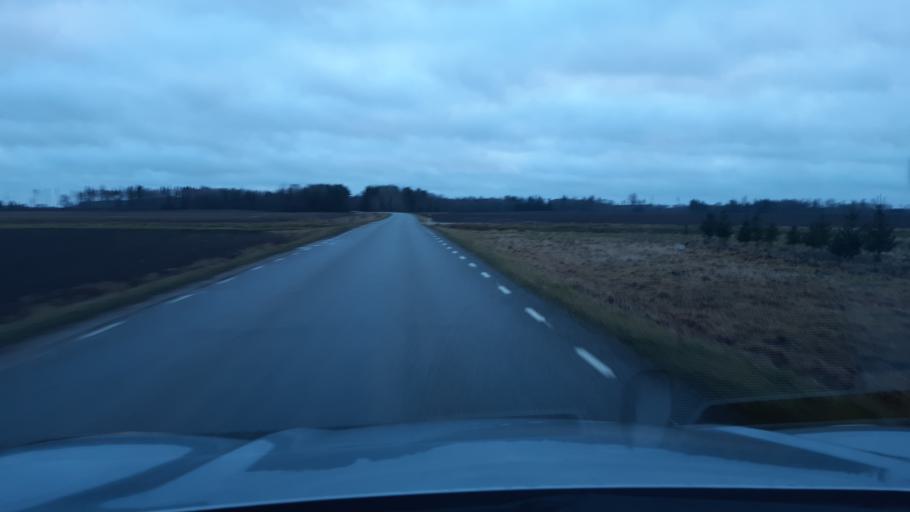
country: EE
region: Raplamaa
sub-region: Rapla vald
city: Rapla
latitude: 59.0358
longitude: 24.6776
